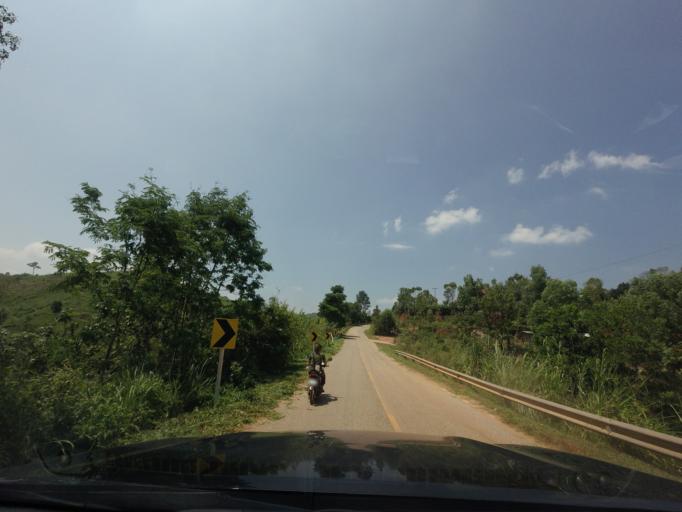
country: TH
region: Loei
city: Na Haeo
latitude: 17.5946
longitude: 100.9063
